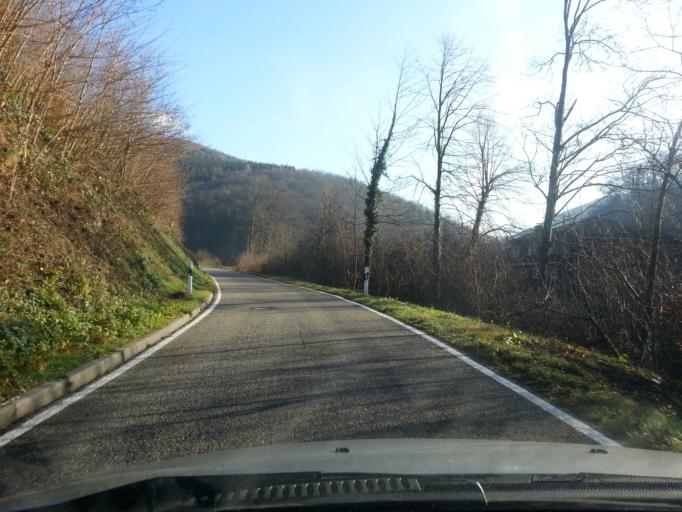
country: DE
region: Baden-Wuerttemberg
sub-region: Karlsruhe Region
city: Eberbach
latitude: 49.4911
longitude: 9.0467
